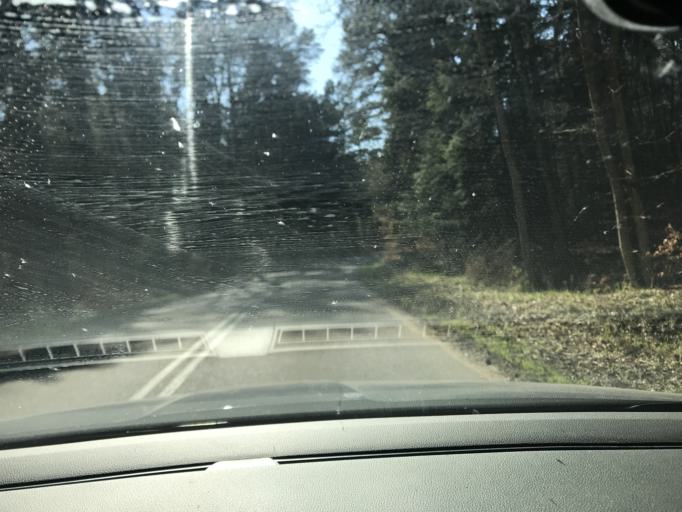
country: PL
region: Pomeranian Voivodeship
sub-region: Powiat nowodworski
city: Krynica Morska
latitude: 54.3669
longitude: 19.3829
